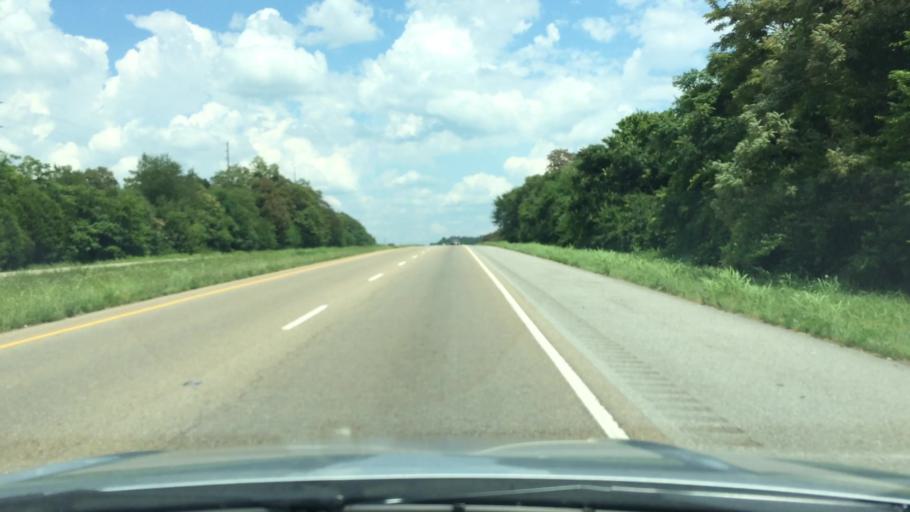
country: US
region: Tennessee
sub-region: Hamblen County
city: Morristown
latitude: 36.1799
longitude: -83.3340
